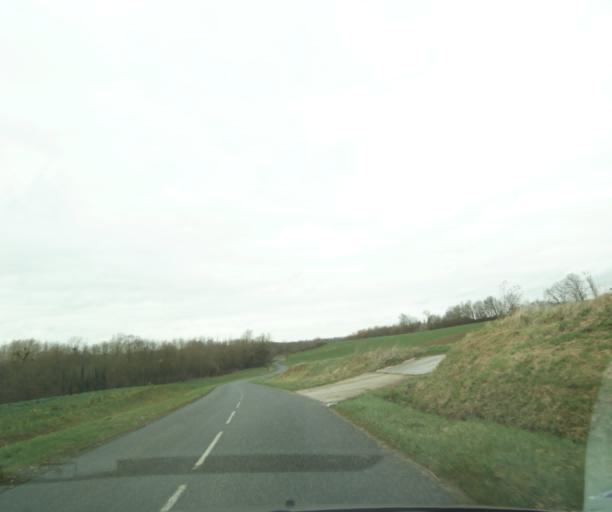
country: FR
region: Picardie
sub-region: Departement de l'Oise
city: Noyon
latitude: 49.5943
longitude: 2.9927
